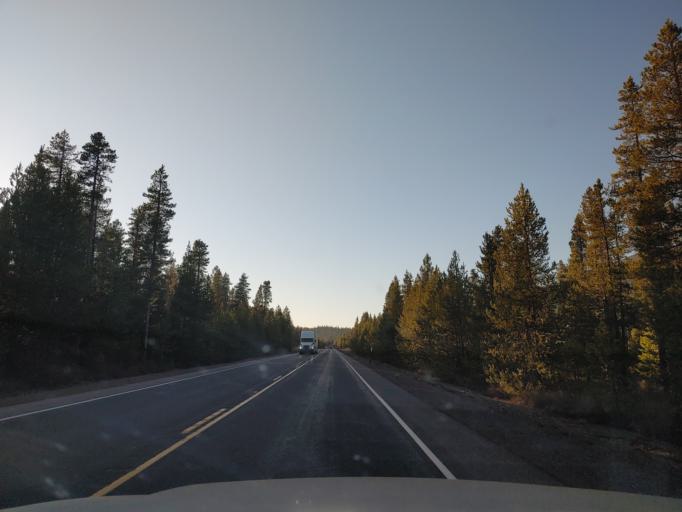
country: US
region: Oregon
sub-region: Deschutes County
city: La Pine
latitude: 43.4324
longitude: -121.8554
